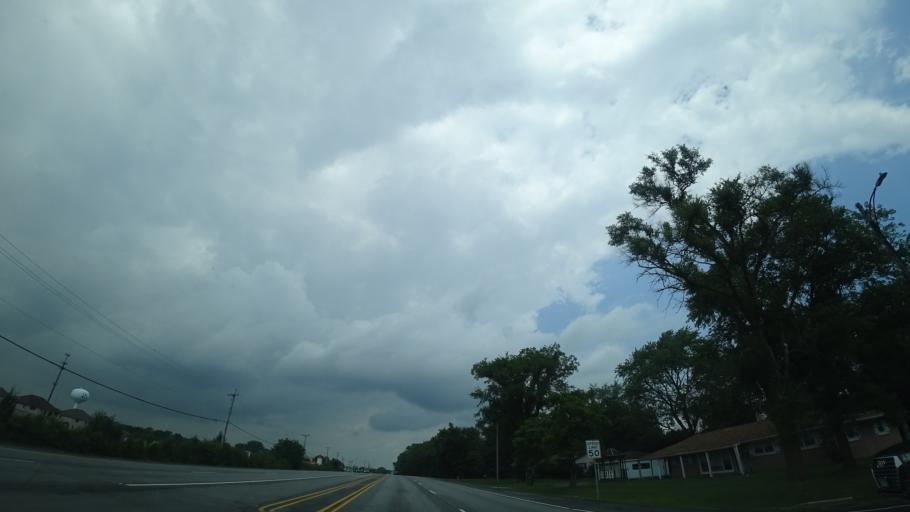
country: US
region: Illinois
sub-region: Cook County
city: Country Club Hills
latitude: 41.5532
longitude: -87.7328
